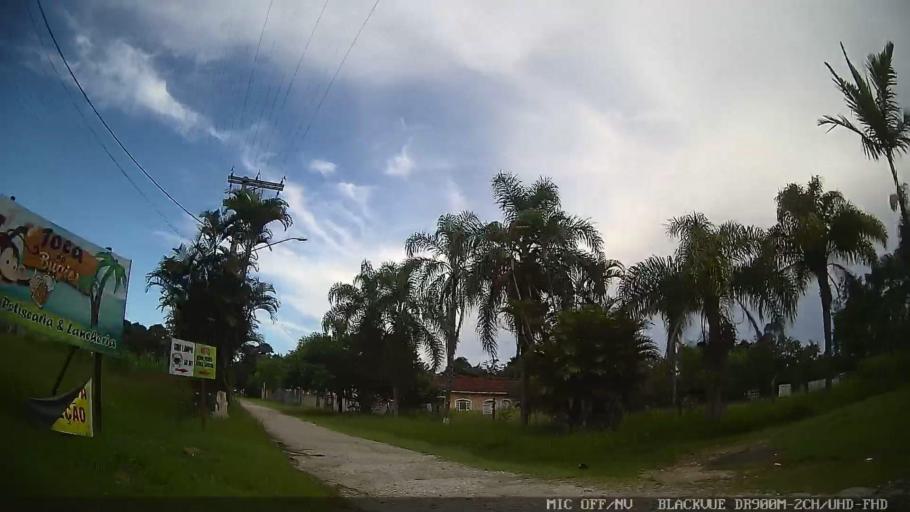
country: BR
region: Sao Paulo
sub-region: Iguape
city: Iguape
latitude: -24.6883
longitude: -47.5167
